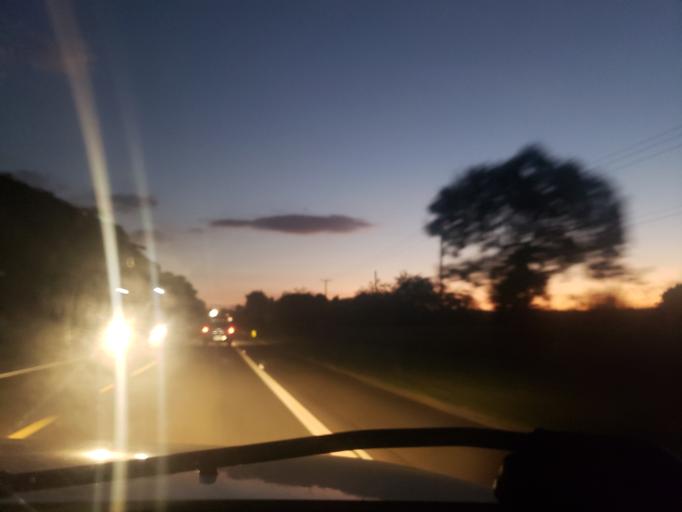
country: BR
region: Sao Paulo
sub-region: Conchal
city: Conchal
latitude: -22.3233
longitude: -47.1428
